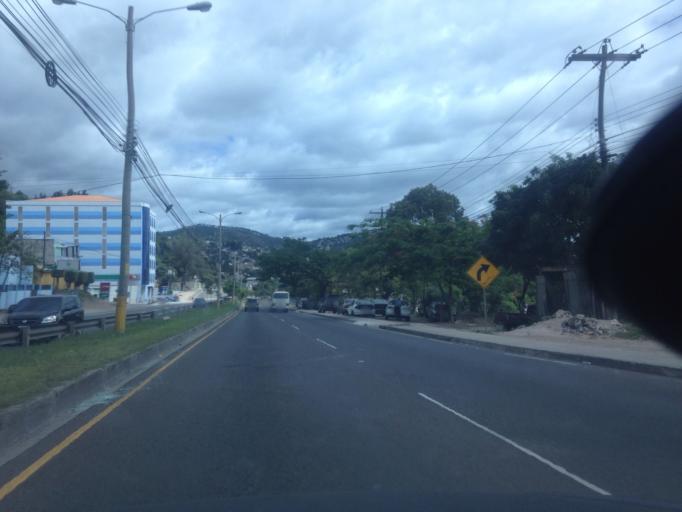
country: HN
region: Francisco Morazan
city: Tegucigalpa
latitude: 14.0747
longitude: -87.1661
